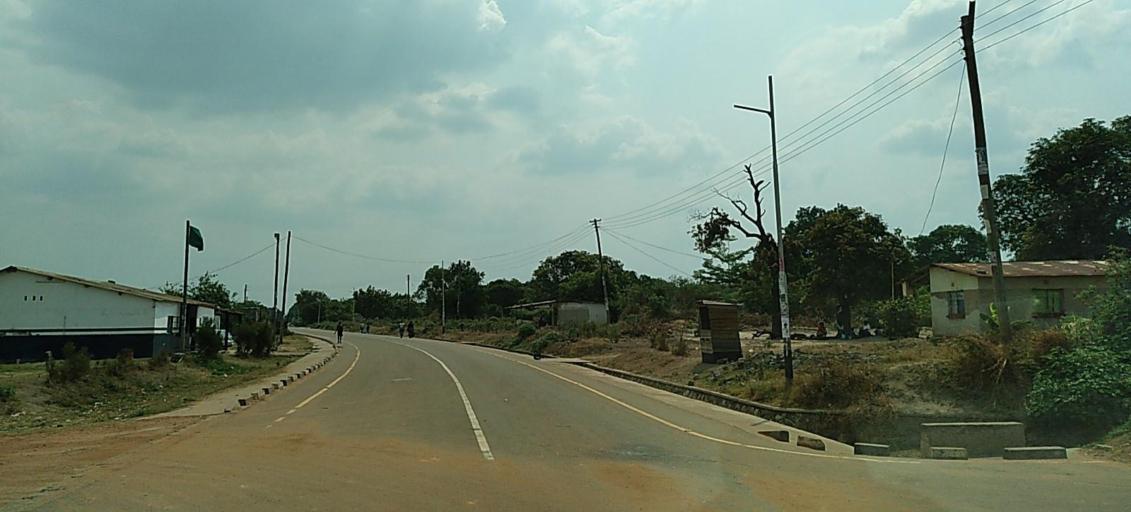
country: ZM
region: Copperbelt
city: Kalulushi
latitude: -12.8545
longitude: 28.1384
